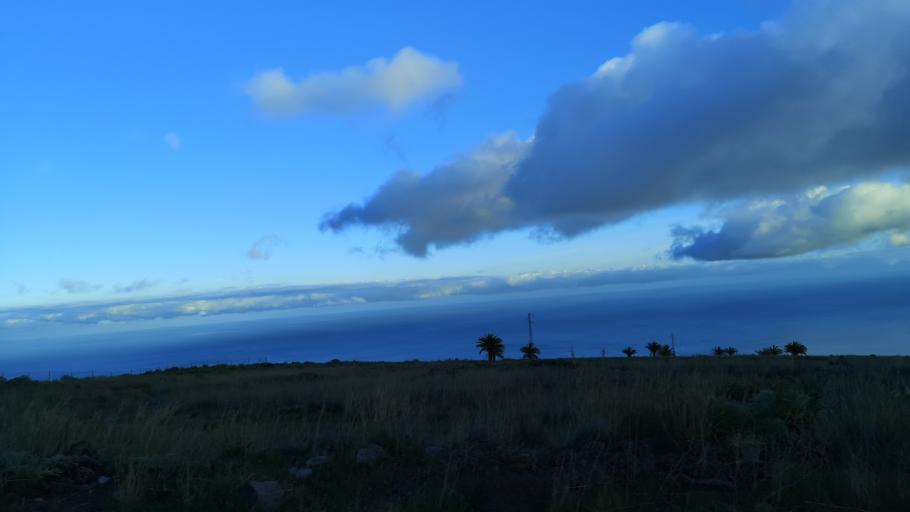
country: ES
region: Canary Islands
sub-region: Provincia de Santa Cruz de Tenerife
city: Alajero
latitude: 28.0499
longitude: -17.2320
